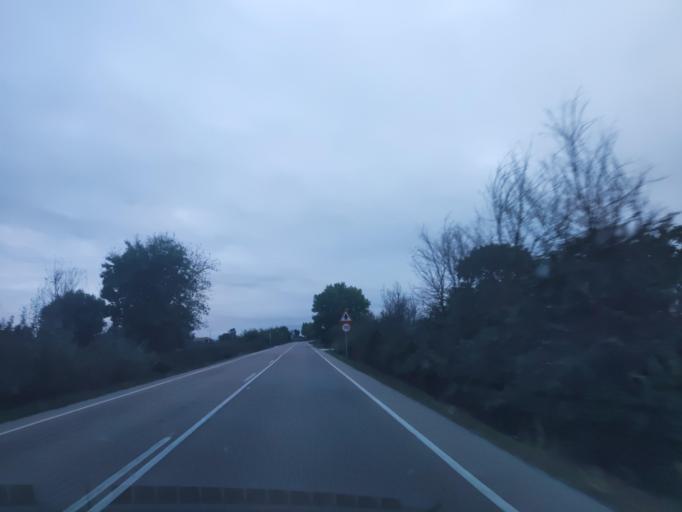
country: ES
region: Castille and Leon
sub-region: Provincia de Salamanca
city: Lumbrales
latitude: 40.9359
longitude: -6.7277
